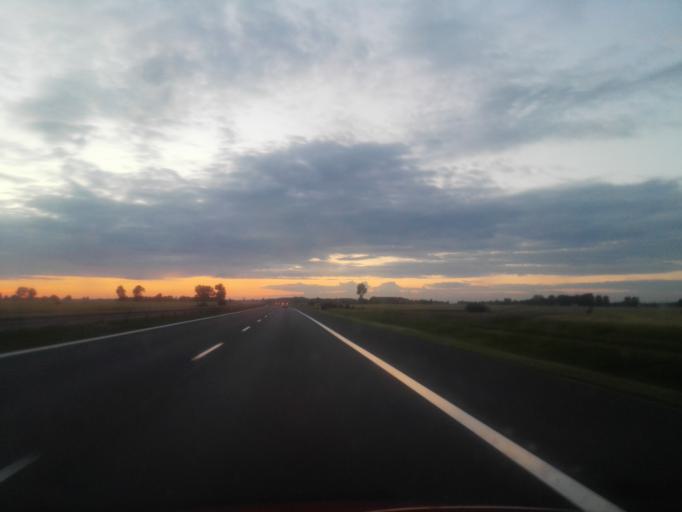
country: PL
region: Lodz Voivodeship
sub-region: Piotrkow Trybunalski
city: Piotrkow Trybunalski
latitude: 51.4610
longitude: 19.6380
